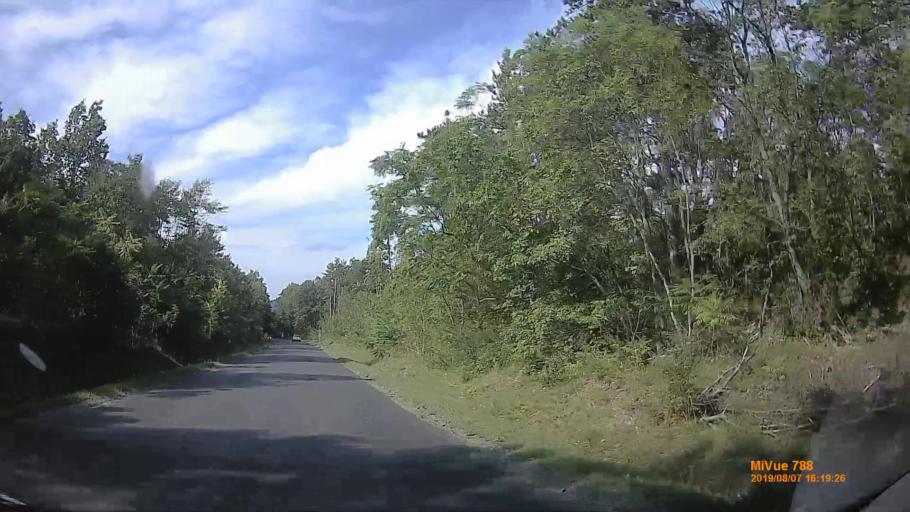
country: HU
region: Zala
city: Cserszegtomaj
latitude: 46.8518
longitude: 17.2673
